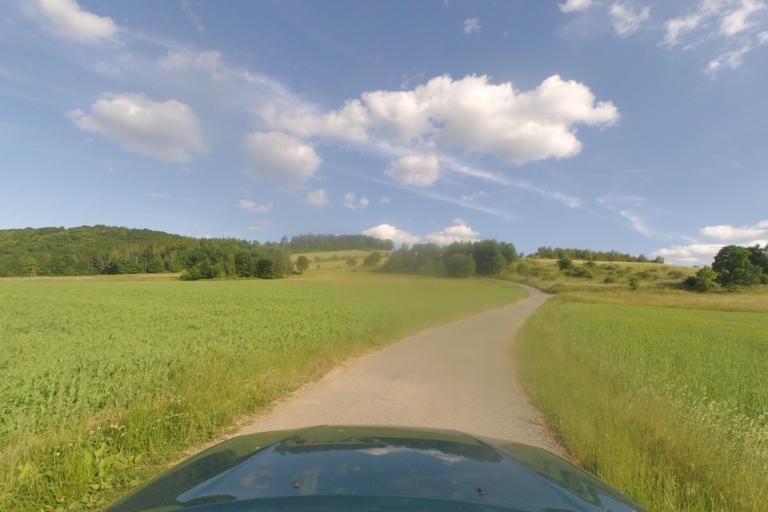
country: PL
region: Lower Silesian Voivodeship
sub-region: Powiat zabkowicki
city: Bardo
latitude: 50.4925
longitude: 16.6952
